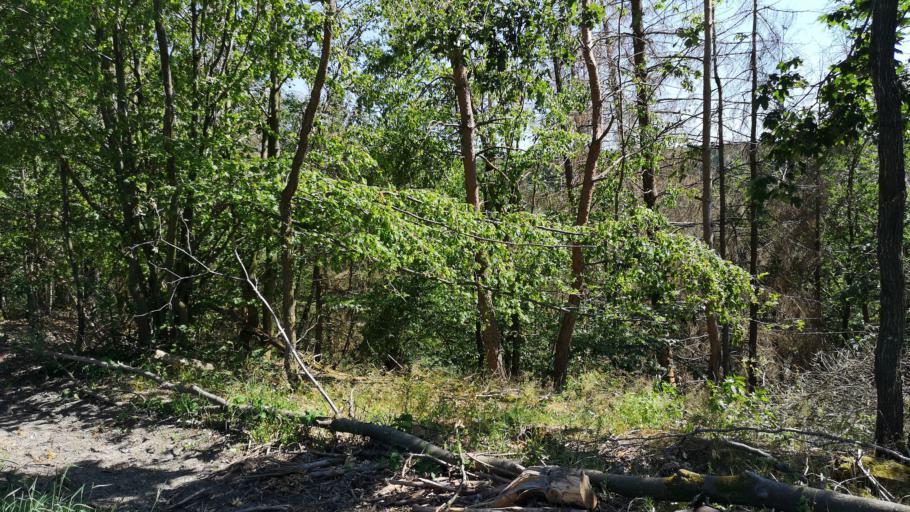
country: DE
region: Saxony-Anhalt
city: Uftrungen
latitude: 51.5262
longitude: 11.0224
